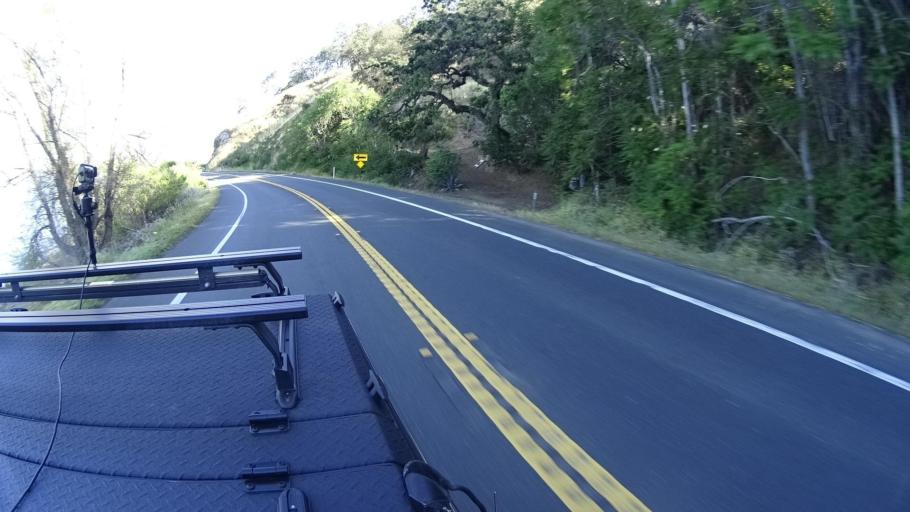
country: US
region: California
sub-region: Lake County
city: Lucerne
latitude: 39.0615
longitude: -122.7826
